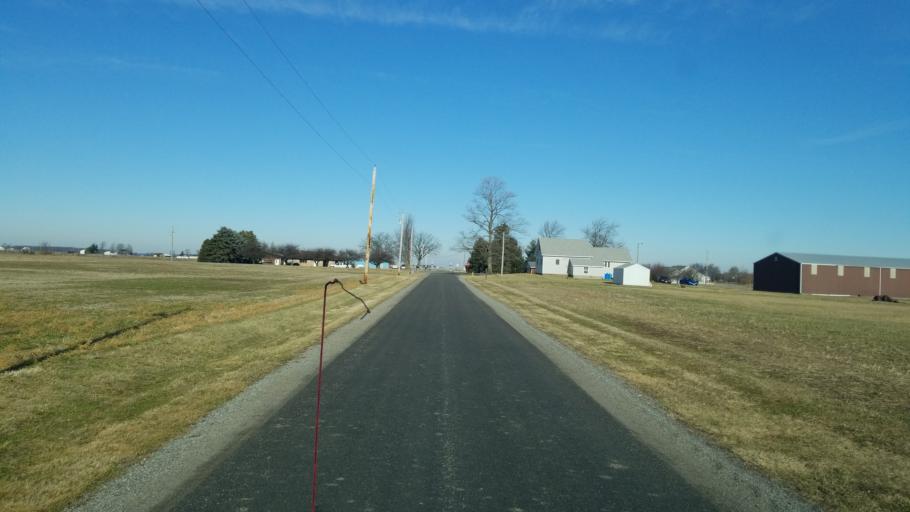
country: US
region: Ohio
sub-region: Putnam County
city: Leipsic
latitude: 41.0998
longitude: -84.0087
